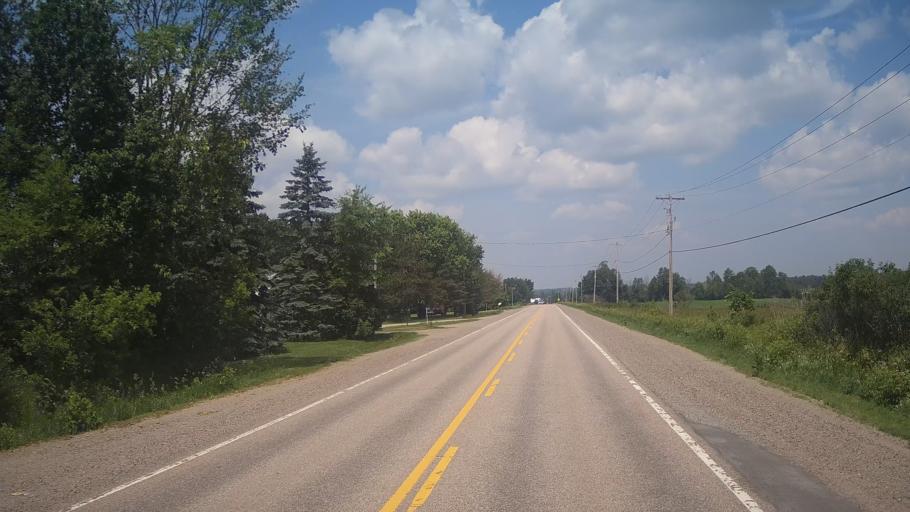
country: CA
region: Quebec
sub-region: Outaouais
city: Shawville
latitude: 45.5778
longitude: -76.4491
